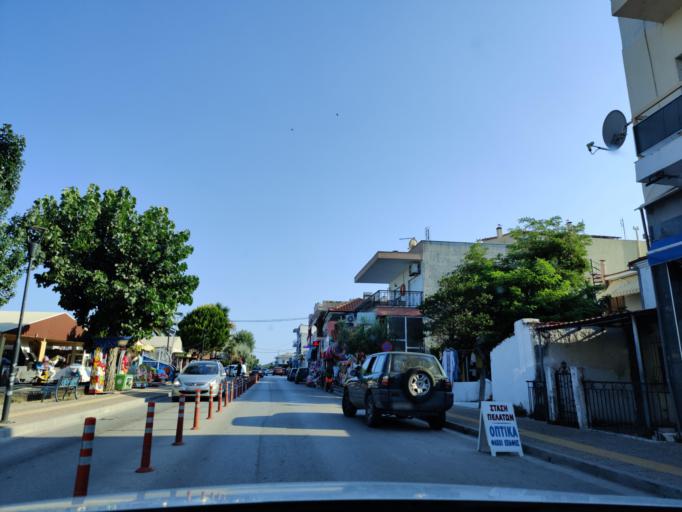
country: GR
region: East Macedonia and Thrace
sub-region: Nomos Kavalas
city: Nea Peramos
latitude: 40.8394
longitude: 24.3050
